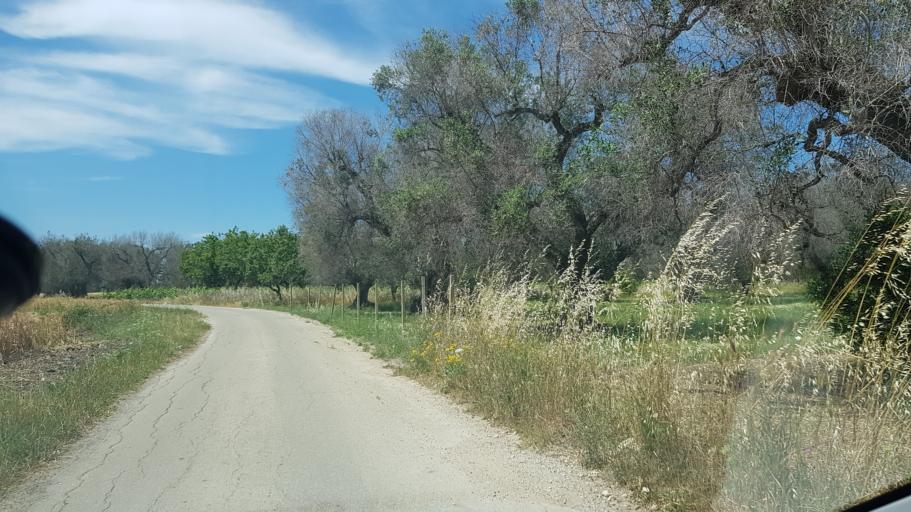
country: IT
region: Apulia
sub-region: Provincia di Brindisi
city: San Pietro Vernotico
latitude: 40.5302
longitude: 18.0012
